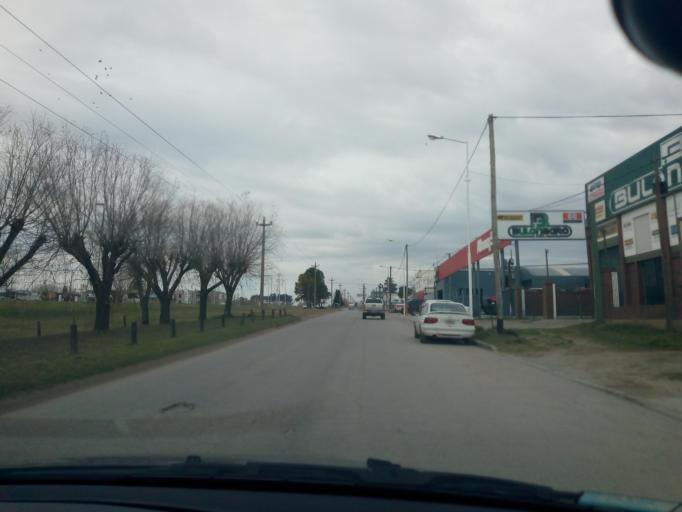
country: AR
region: Buenos Aires
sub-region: Partido de Tandil
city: Tandil
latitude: -37.3167
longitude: -59.1083
